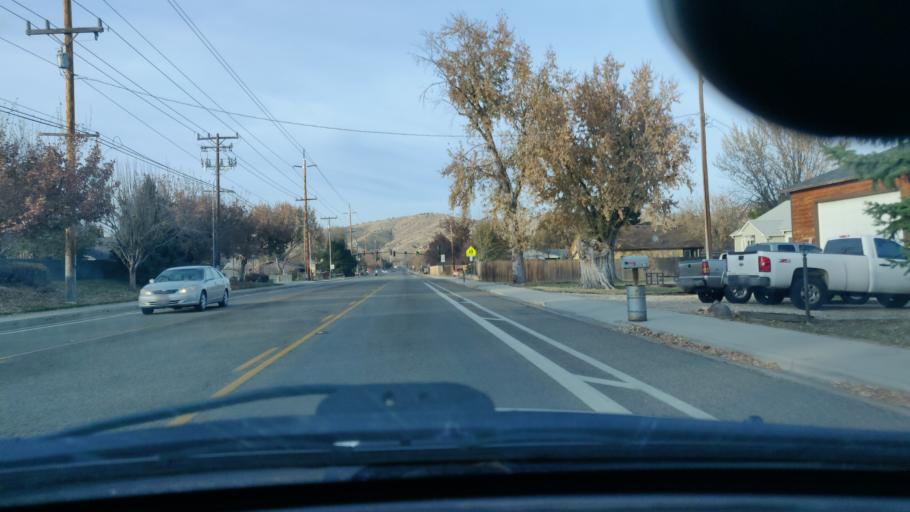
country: US
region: Idaho
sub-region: Ada County
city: Garden City
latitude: 43.6762
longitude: -116.2792
